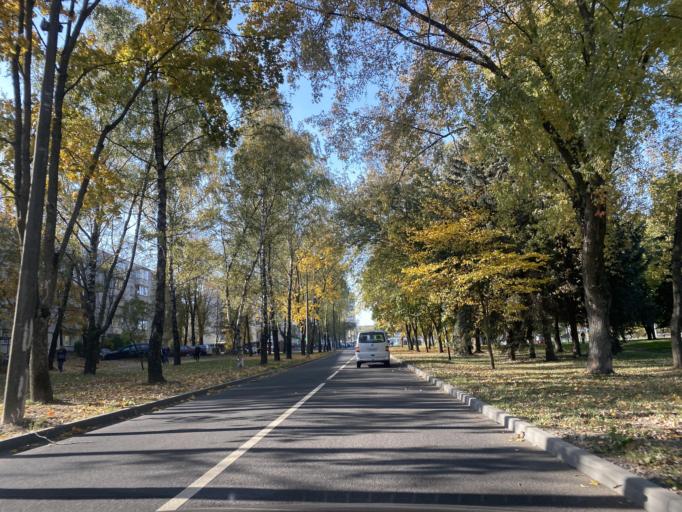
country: BY
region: Minsk
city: Borovlyany
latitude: 53.9531
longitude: 27.6238
